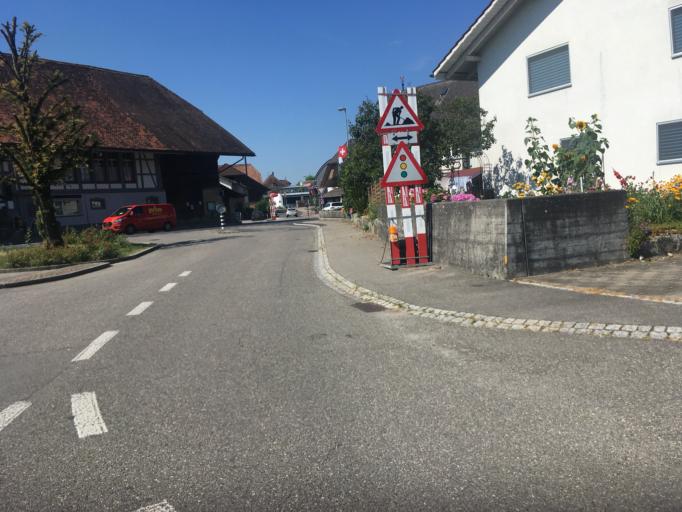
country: CH
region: Bern
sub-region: Bern-Mittelland District
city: Fraubrunnen
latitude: 47.0736
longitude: 7.5514
